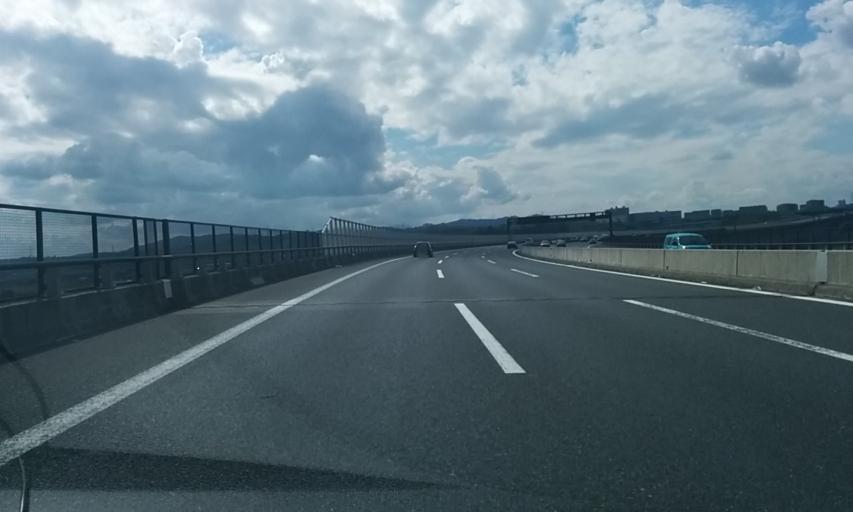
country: JP
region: Kyoto
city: Yawata
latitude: 34.8552
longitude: 135.7344
